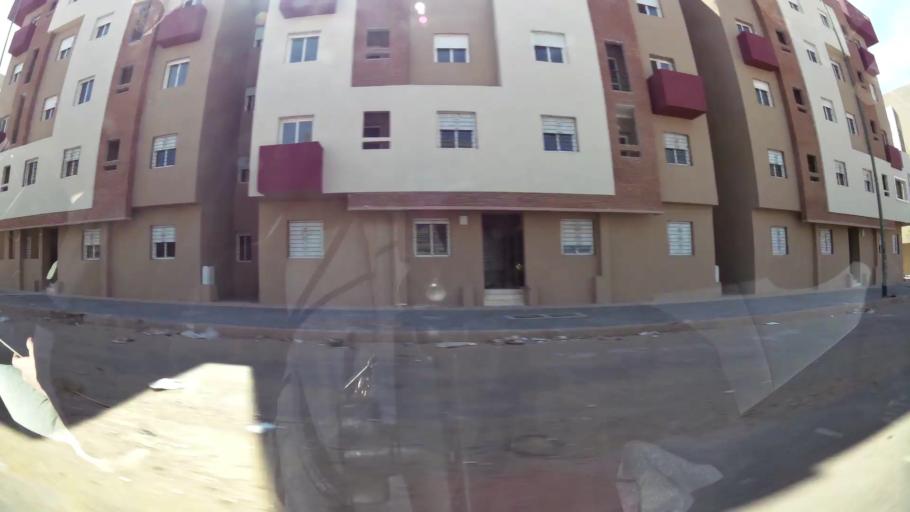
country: MA
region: Marrakech-Tensift-Al Haouz
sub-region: Marrakech
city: Marrakesh
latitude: 31.6310
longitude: -8.0729
